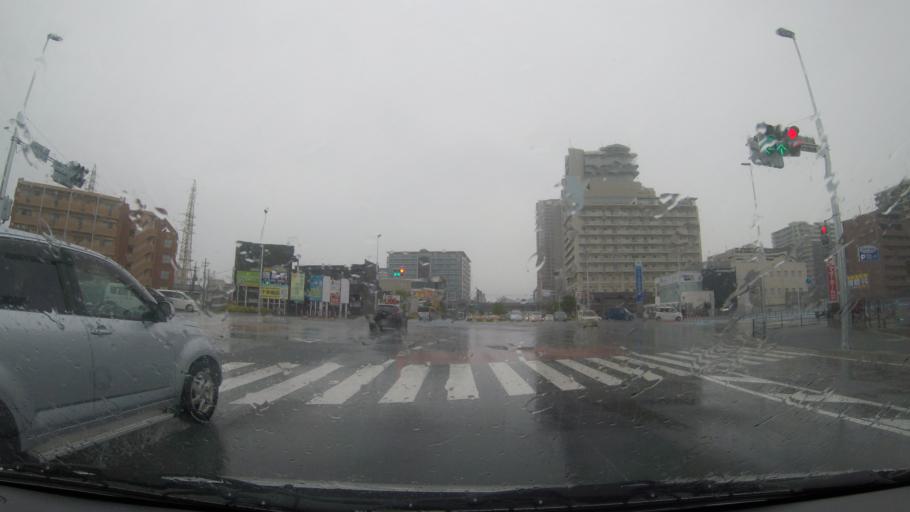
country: JP
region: Fukuoka
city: Fukuoka-shi
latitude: 33.6469
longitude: 130.4411
